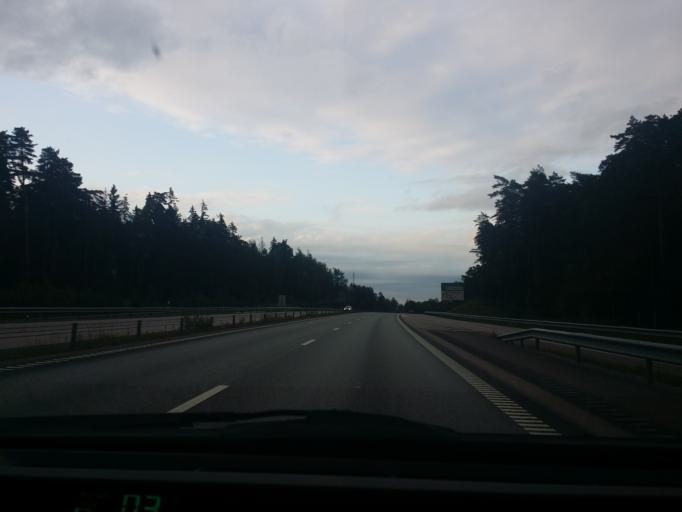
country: SE
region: Vaestmanland
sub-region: Vasteras
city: Vasteras
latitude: 59.6008
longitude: 16.4390
